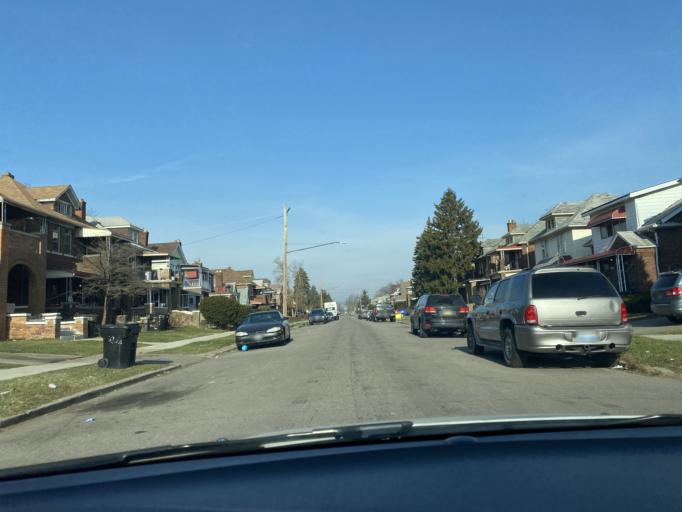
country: US
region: Michigan
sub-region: Wayne County
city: Highland Park
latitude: 42.3774
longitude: -83.1413
